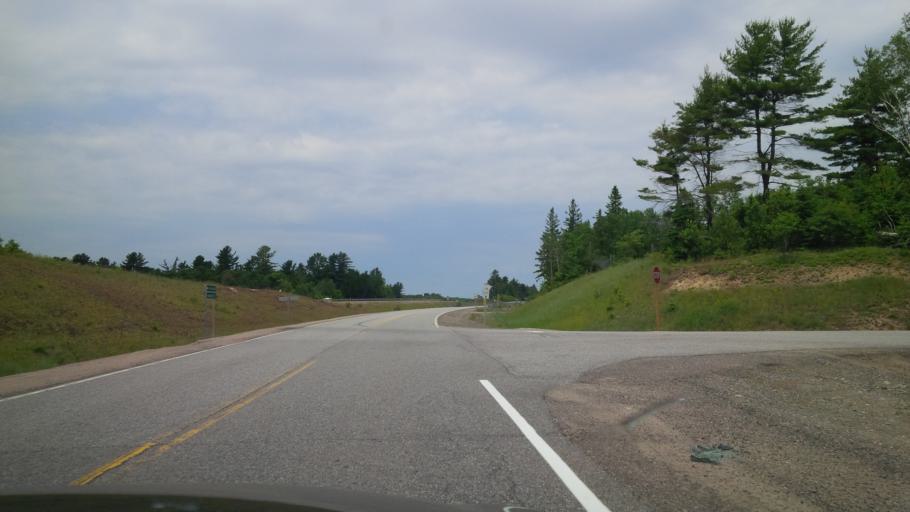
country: CA
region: Ontario
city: Huntsville
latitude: 45.5142
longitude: -79.3072
